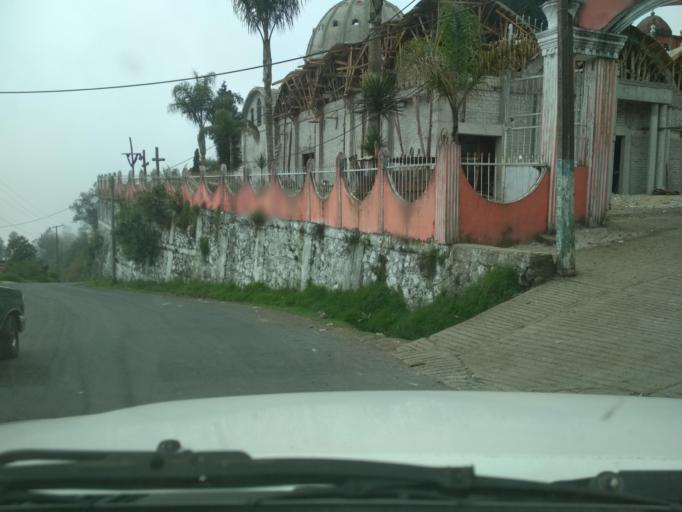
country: MX
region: Veracruz
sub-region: La Perla
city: Chilapa
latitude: 18.9653
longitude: -97.1687
